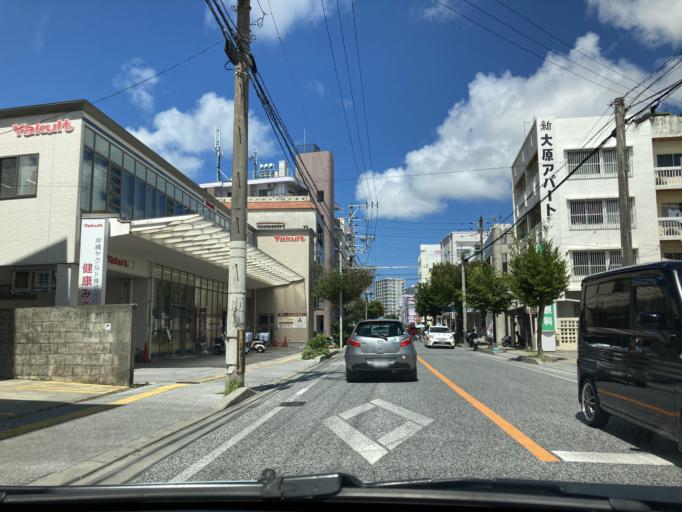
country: JP
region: Okinawa
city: Naha-shi
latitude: 26.2086
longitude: 127.6989
